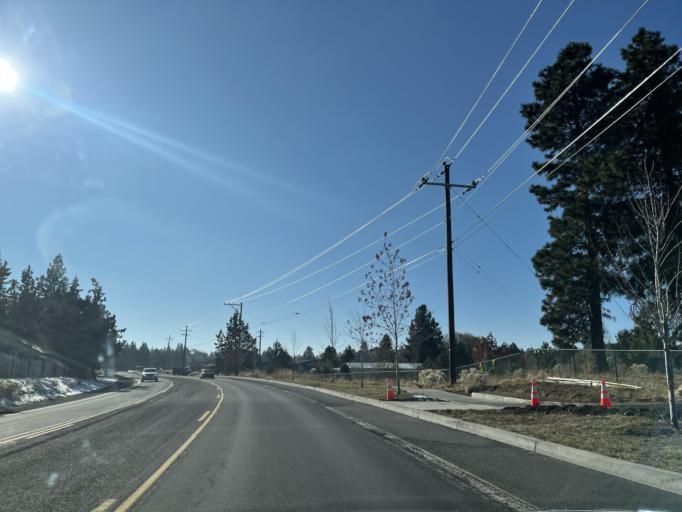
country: US
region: Oregon
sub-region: Deschutes County
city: Bend
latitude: 44.0809
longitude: -121.2815
